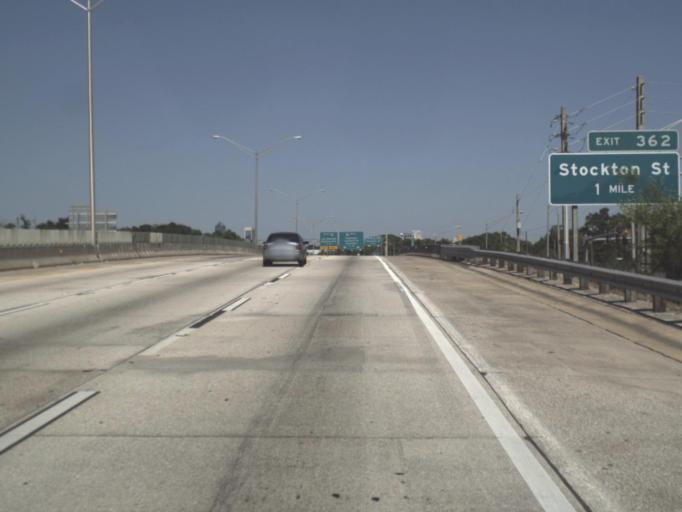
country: US
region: Florida
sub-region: Duval County
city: Jacksonville
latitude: 30.3208
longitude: -81.7063
